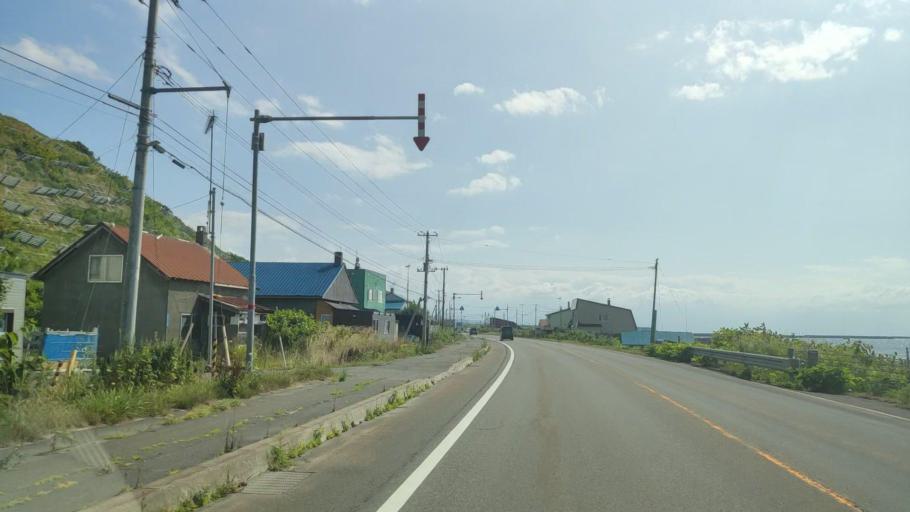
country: JP
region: Hokkaido
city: Rumoi
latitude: 43.9855
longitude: 141.6485
